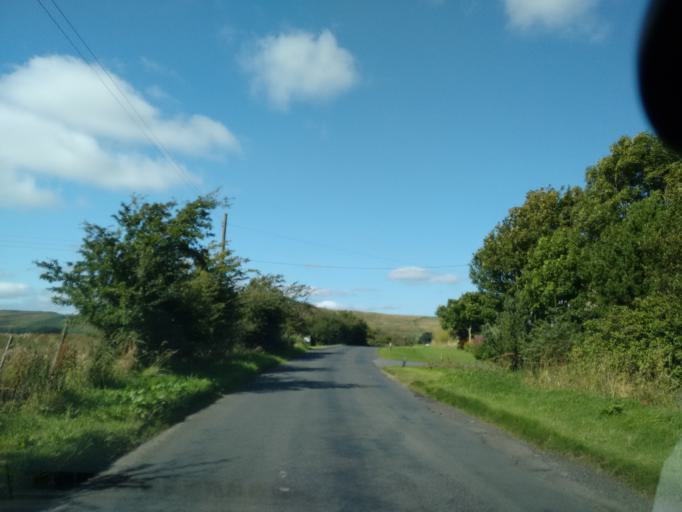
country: GB
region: England
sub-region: Northumberland
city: Bardon Mill
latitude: 54.9903
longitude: -2.3850
